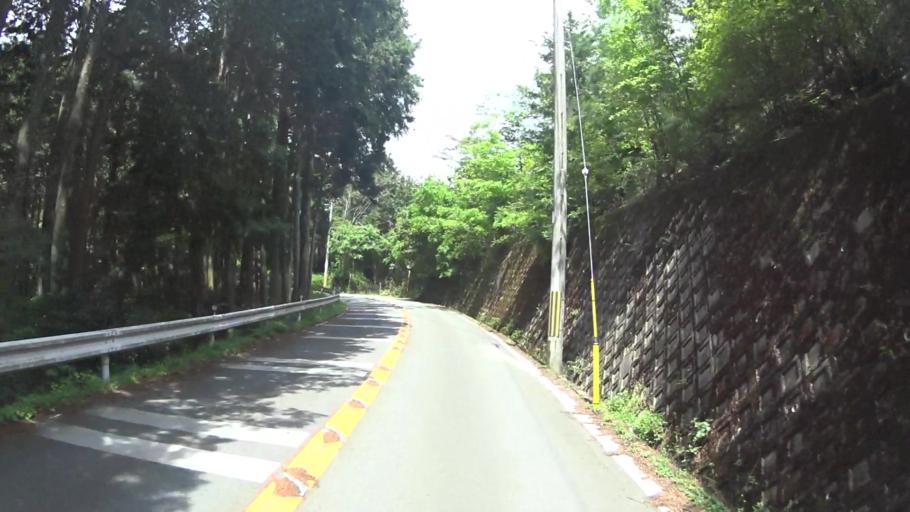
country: JP
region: Kyoto
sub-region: Kyoto-shi
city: Kamigyo-ku
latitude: 35.0622
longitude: 135.7259
